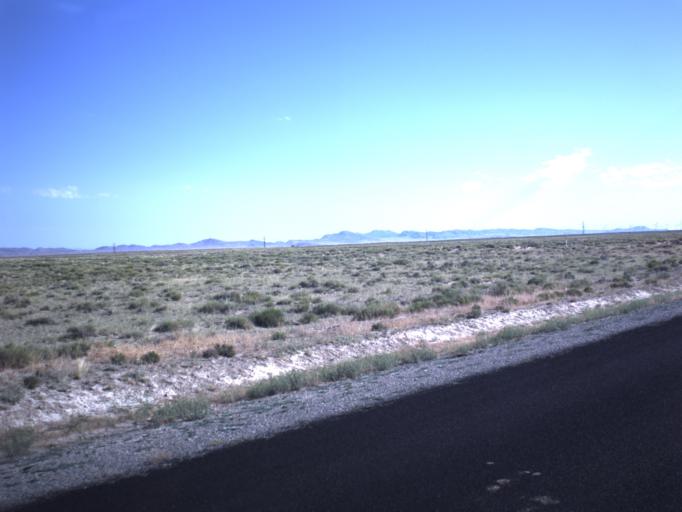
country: US
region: Utah
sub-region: Beaver County
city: Milford
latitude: 38.4693
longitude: -112.9965
